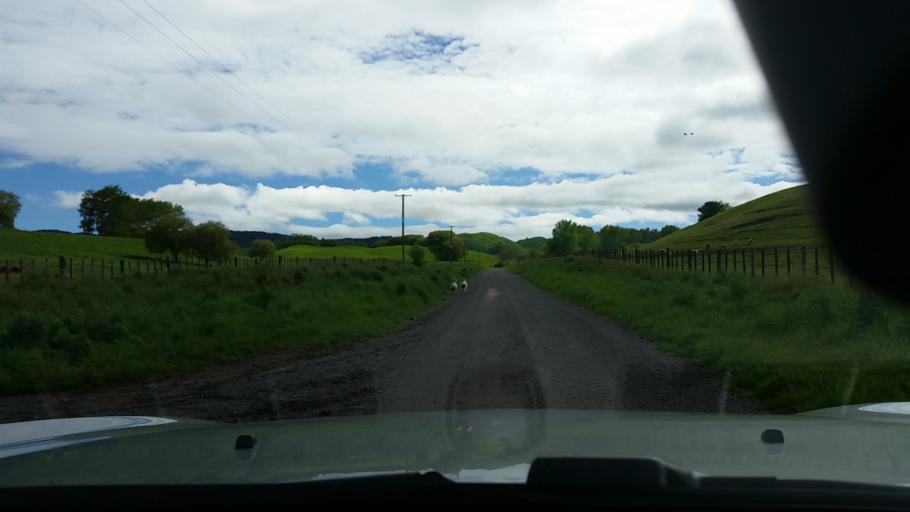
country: NZ
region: Bay of Plenty
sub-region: Rotorua District
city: Rotorua
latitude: -38.3208
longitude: 176.2977
